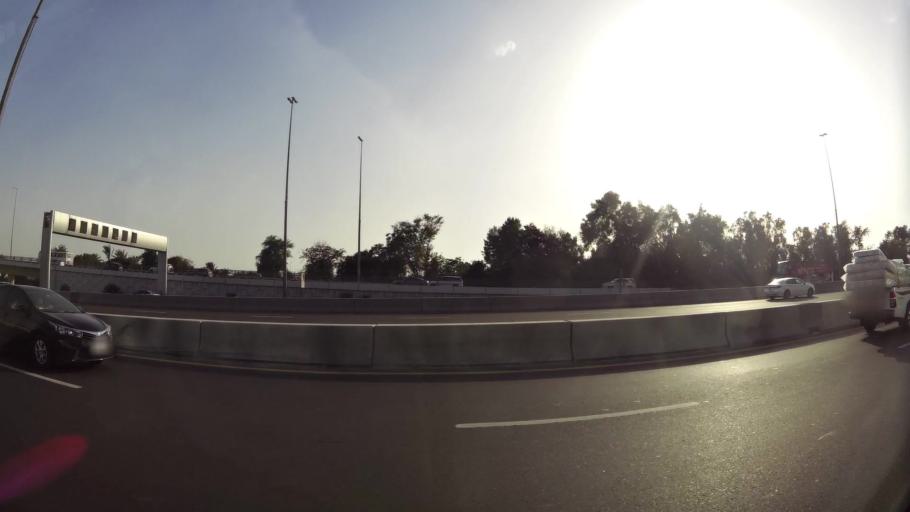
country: AE
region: Ash Shariqah
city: Sharjah
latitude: 25.2428
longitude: 55.3397
